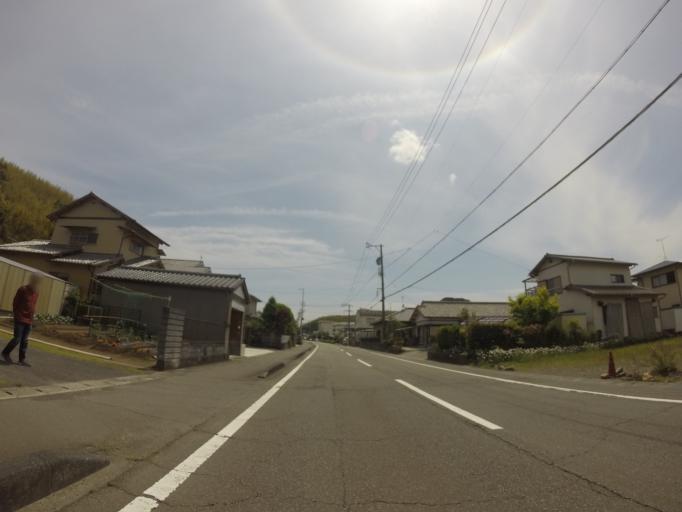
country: JP
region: Shizuoka
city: Fujieda
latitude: 34.8969
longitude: 138.2477
